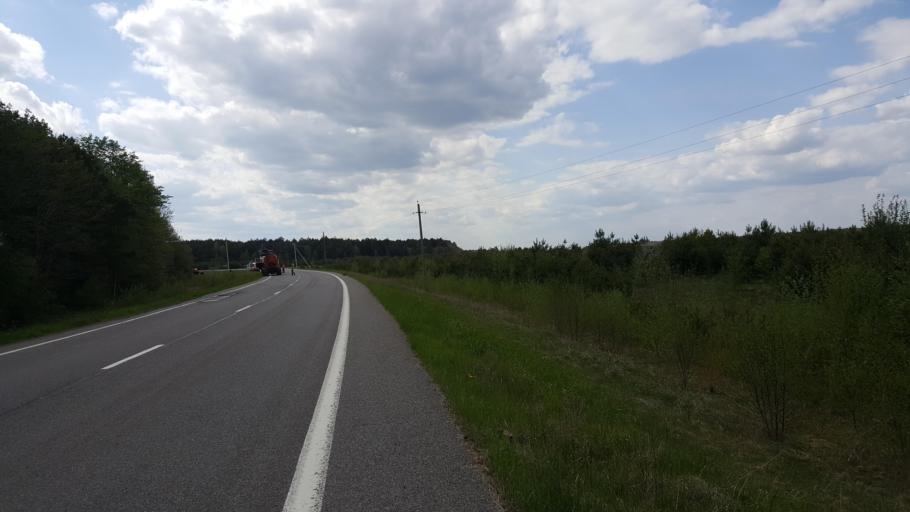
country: BY
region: Brest
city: Kamyanyets
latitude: 52.4023
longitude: 24.0008
